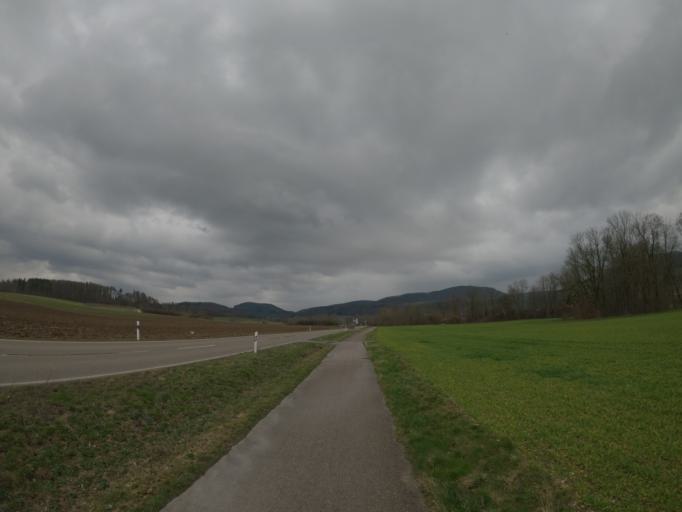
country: DE
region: Baden-Wuerttemberg
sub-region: Regierungsbezirk Stuttgart
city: Schlat
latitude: 48.6642
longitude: 9.7000
